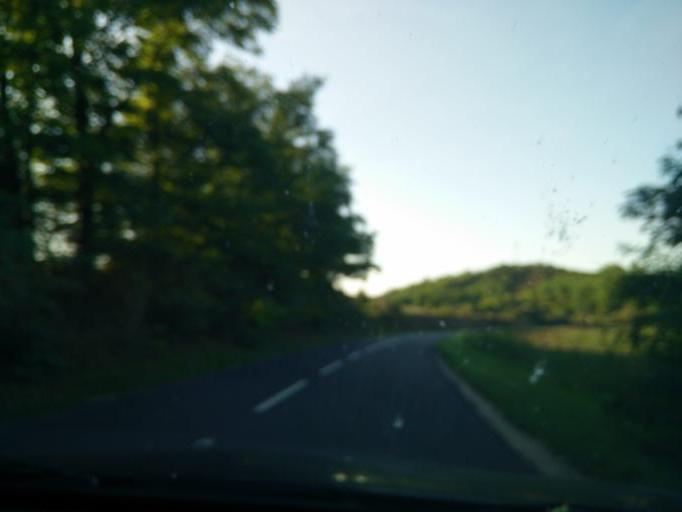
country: HU
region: Pest
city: Piliscsaba
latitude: 47.6466
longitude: 18.7820
